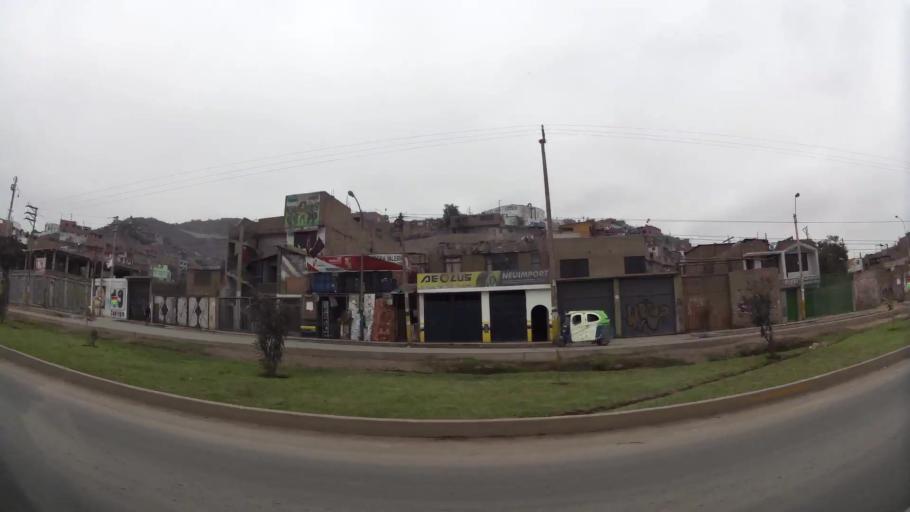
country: PE
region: Lima
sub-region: Lima
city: Vitarte
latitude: -12.0422
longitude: -76.9255
